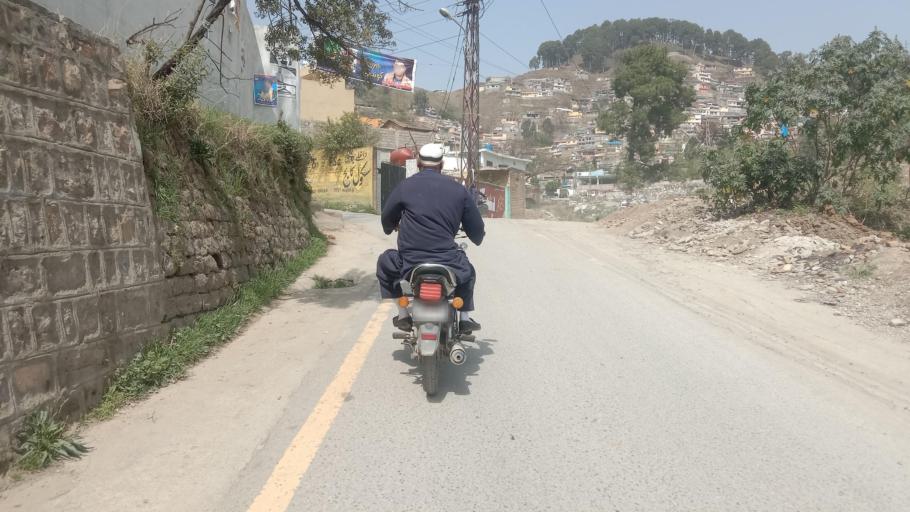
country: PK
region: Khyber Pakhtunkhwa
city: Abbottabad
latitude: 34.1483
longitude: 73.2023
